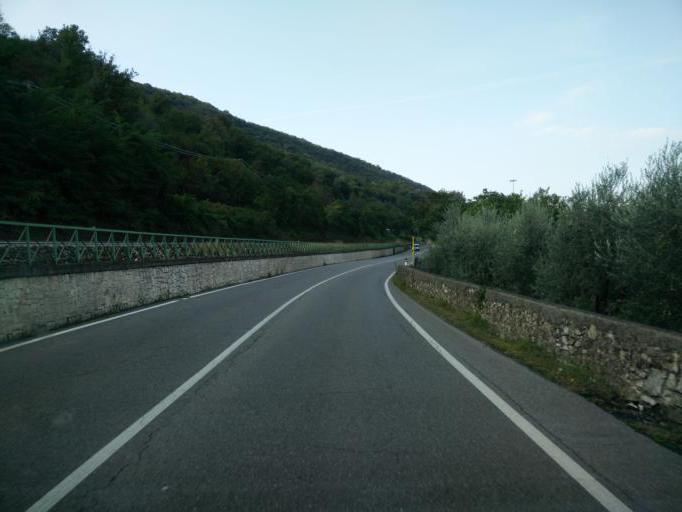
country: IT
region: Lombardy
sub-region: Provincia di Brescia
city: Iseo
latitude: 45.6502
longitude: 10.0471
